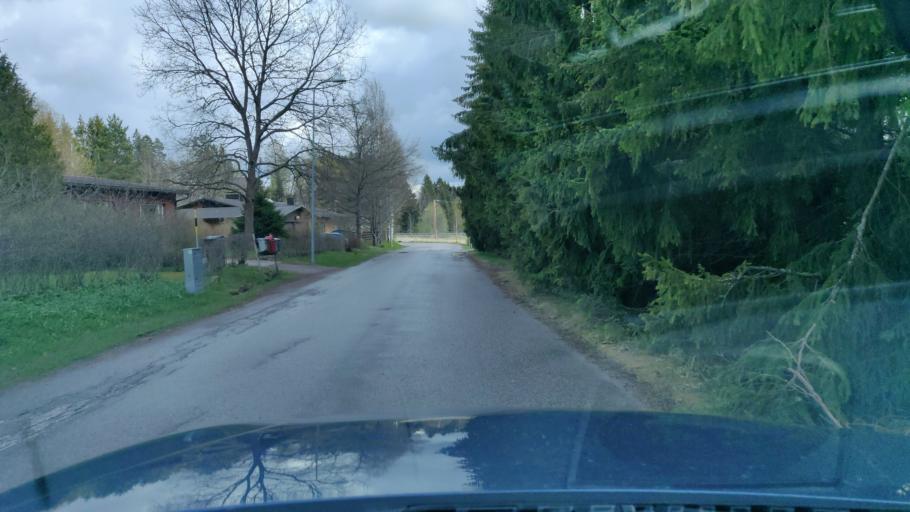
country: FI
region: Uusimaa
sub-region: Helsinki
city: Nurmijaervi
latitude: 60.3621
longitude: 24.7415
